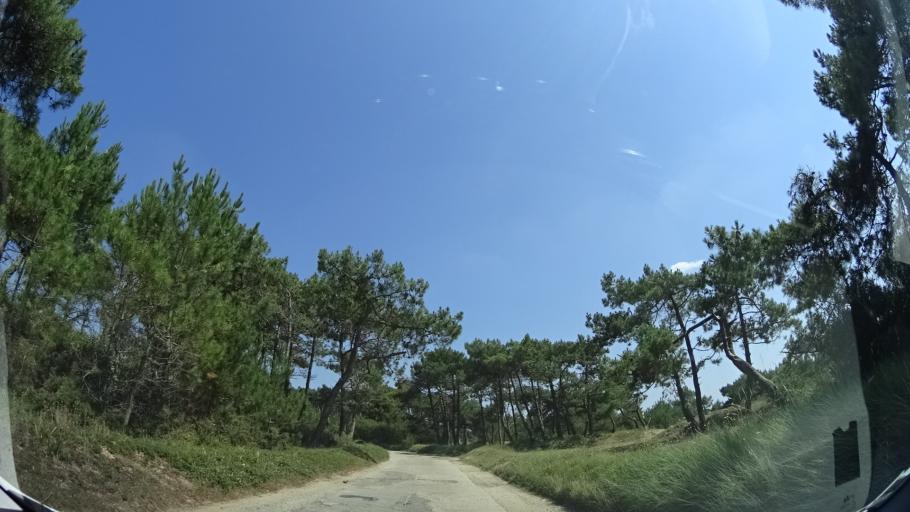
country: FR
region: Brittany
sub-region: Departement du Morbihan
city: Plouharnel
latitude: 47.5951
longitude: -3.1383
